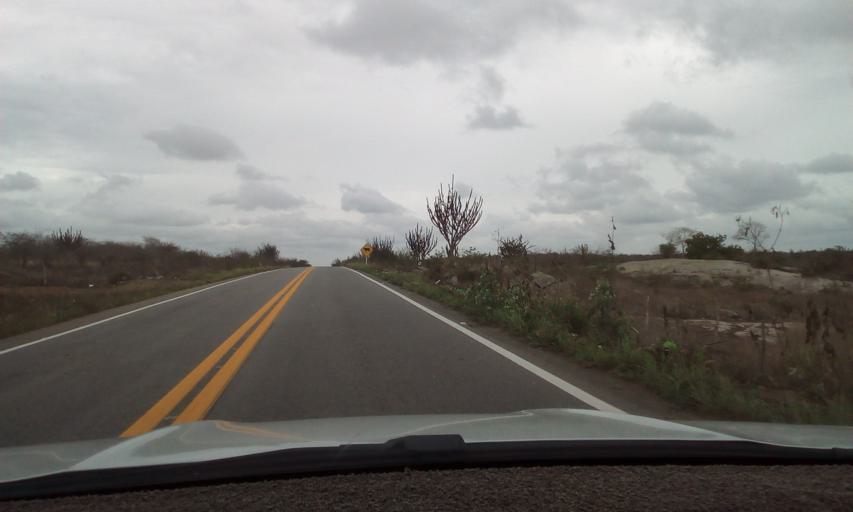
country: BR
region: Paraiba
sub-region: Areia
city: Remigio
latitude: -6.9178
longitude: -35.8516
